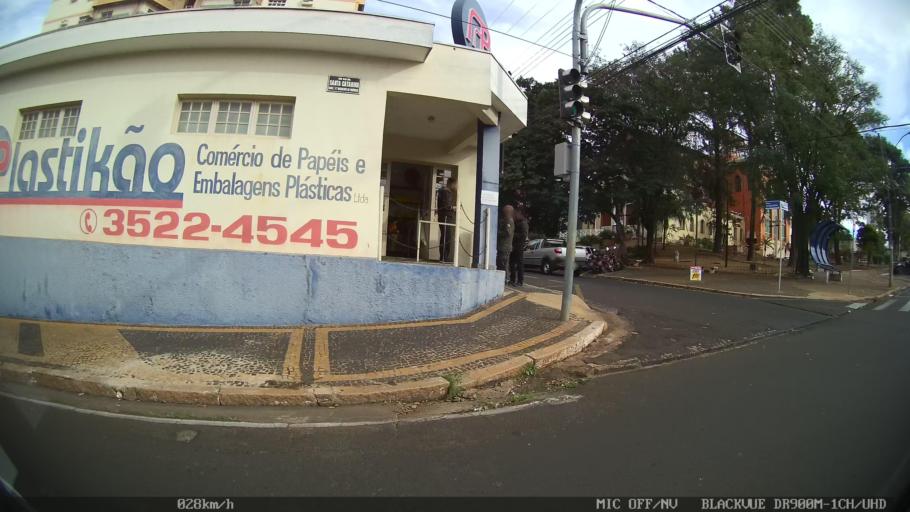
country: BR
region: Sao Paulo
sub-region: Catanduva
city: Catanduva
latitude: -21.1295
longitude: -48.9691
